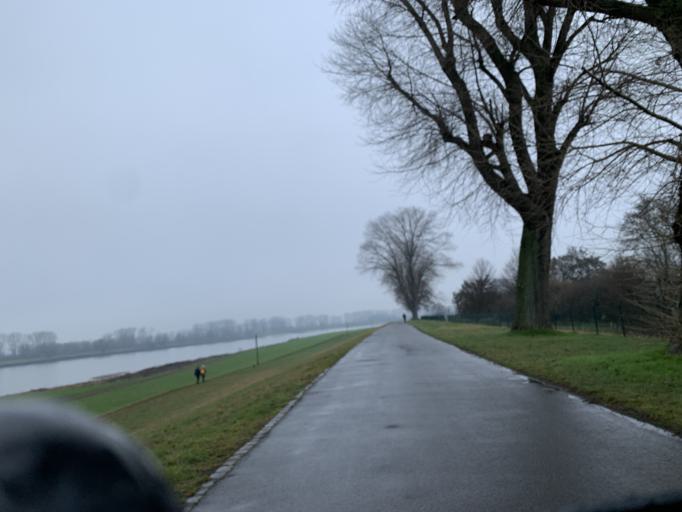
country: DE
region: North Rhine-Westphalia
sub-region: Regierungsbezirk Dusseldorf
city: Meerbusch
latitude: 51.2625
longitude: 6.7174
